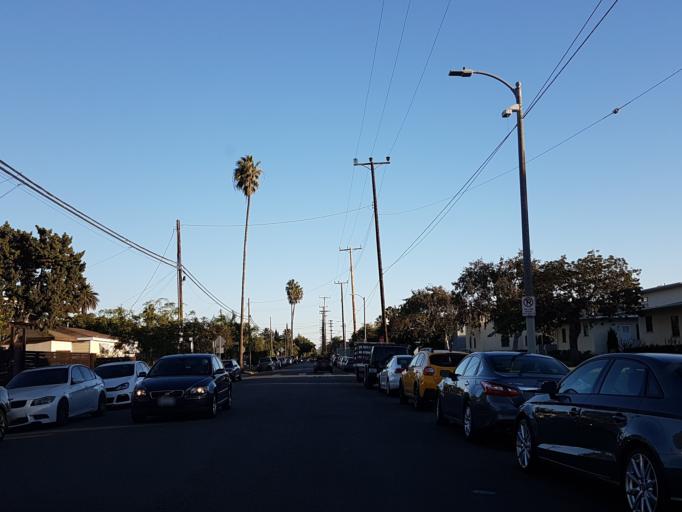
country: US
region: California
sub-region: Los Angeles County
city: Marina del Rey
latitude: 34.0033
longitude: -118.4577
